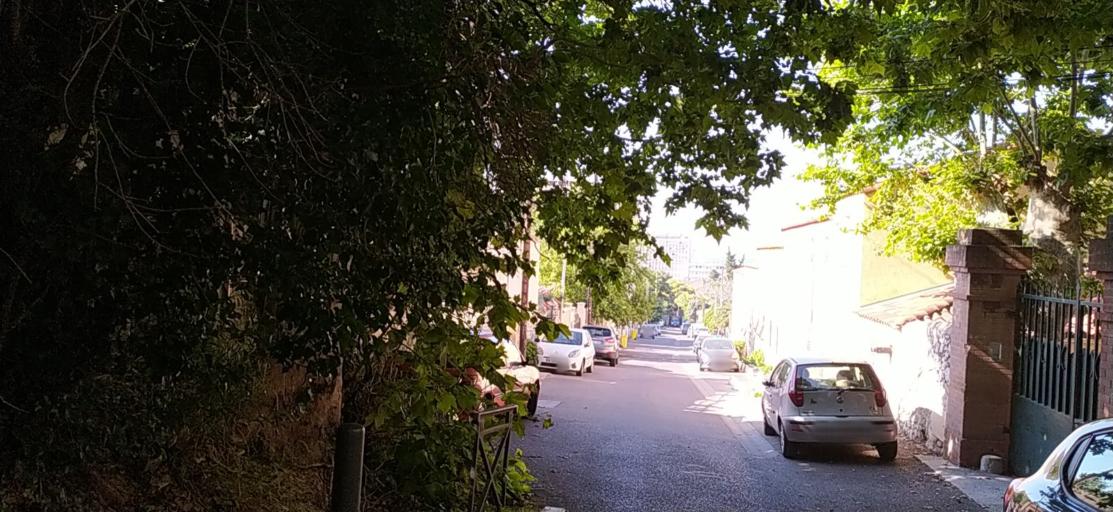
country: FR
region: Provence-Alpes-Cote d'Azur
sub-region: Departement des Bouches-du-Rhone
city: Marseille 16
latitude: 43.3404
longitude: 5.3531
